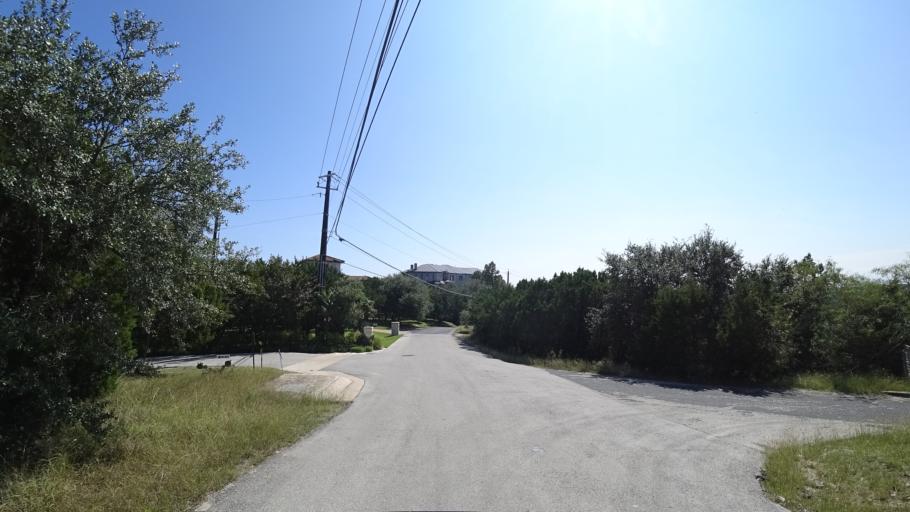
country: US
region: Texas
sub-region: Travis County
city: West Lake Hills
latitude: 30.3039
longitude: -97.7911
